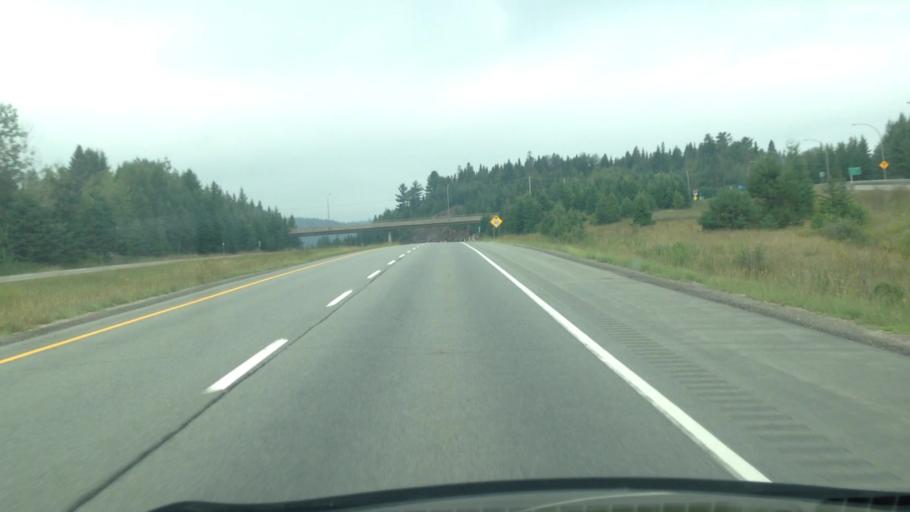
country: CA
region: Quebec
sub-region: Laurentides
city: Sainte-Agathe-des-Monts
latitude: 46.0626
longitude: -74.2852
